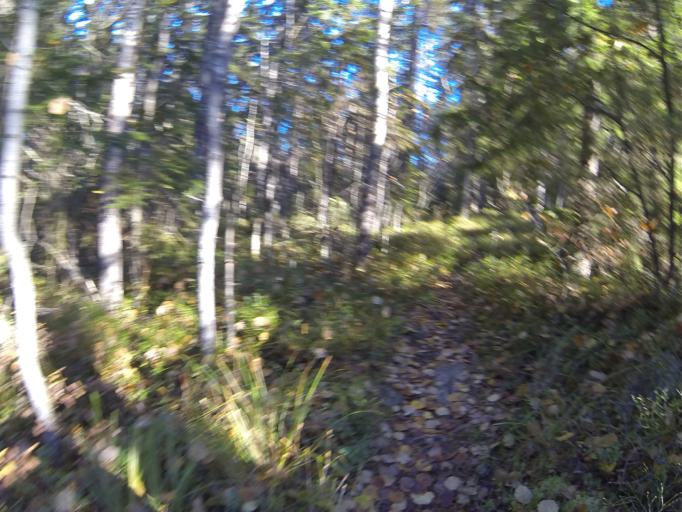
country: FI
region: Varsinais-Suomi
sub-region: Salo
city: Saerkisalo
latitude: 60.2112
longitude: 22.9268
